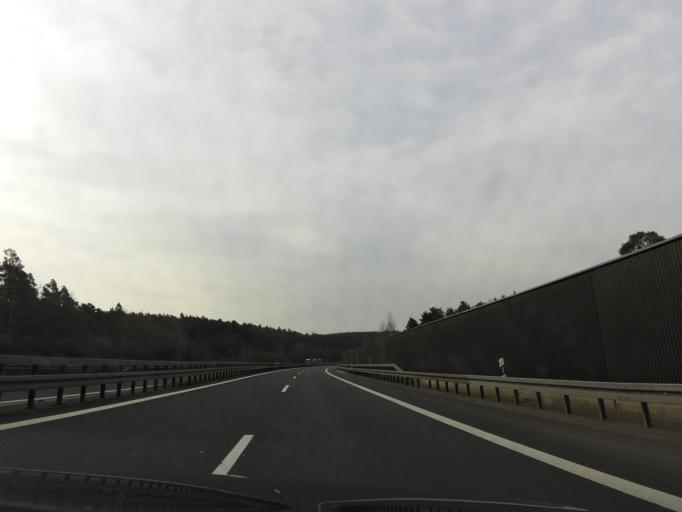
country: DE
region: Bavaria
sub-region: Upper Franconia
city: Zapfendorf
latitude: 50.0237
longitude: 10.9499
